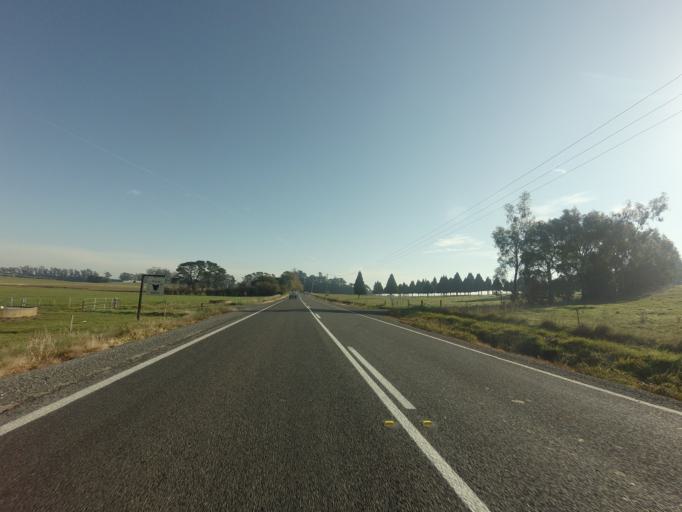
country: AU
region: Tasmania
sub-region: Northern Midlands
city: Longford
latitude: -41.5766
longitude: 147.1023
